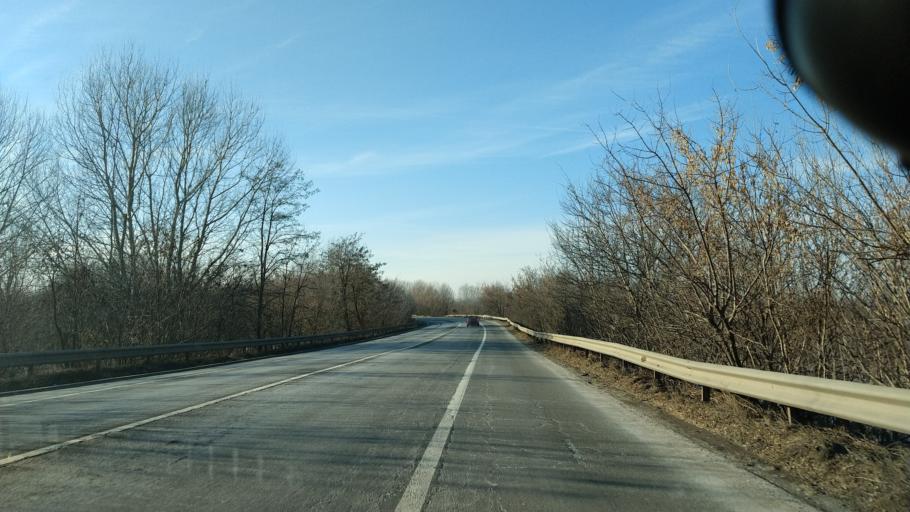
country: RO
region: Iasi
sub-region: Comuna Butea
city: Butea
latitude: 47.0874
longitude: 26.9066
